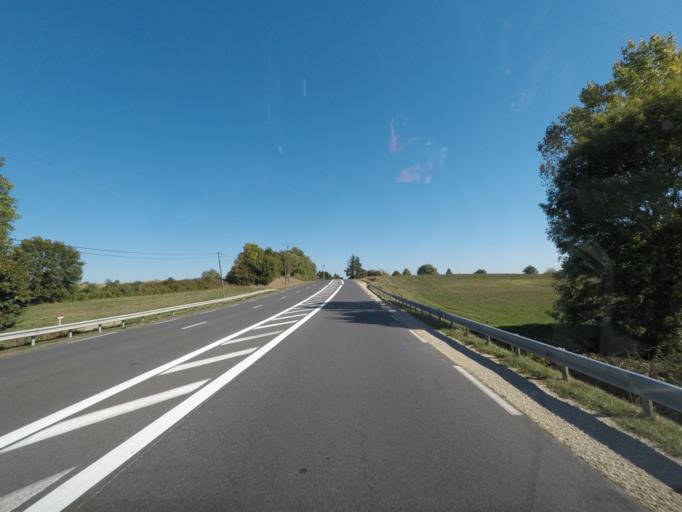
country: FR
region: Rhone-Alpes
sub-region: Departement de l'Ain
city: Saint-Paul-de-Varax
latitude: 46.0934
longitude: 5.1210
